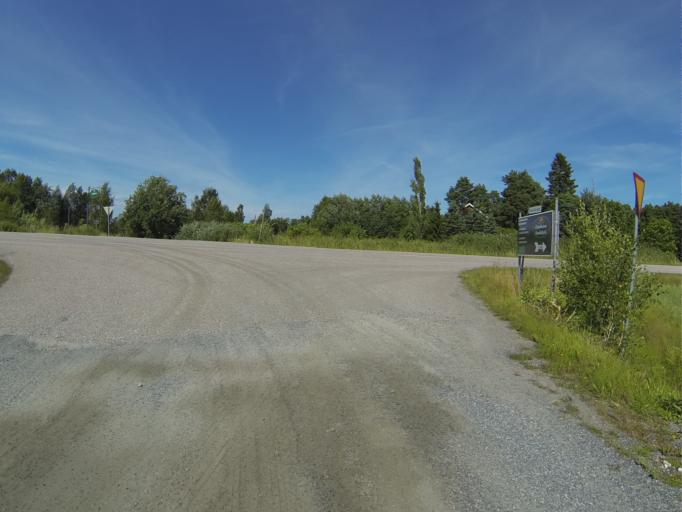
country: FI
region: Varsinais-Suomi
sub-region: Salo
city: Halikko
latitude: 60.2758
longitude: 22.9850
